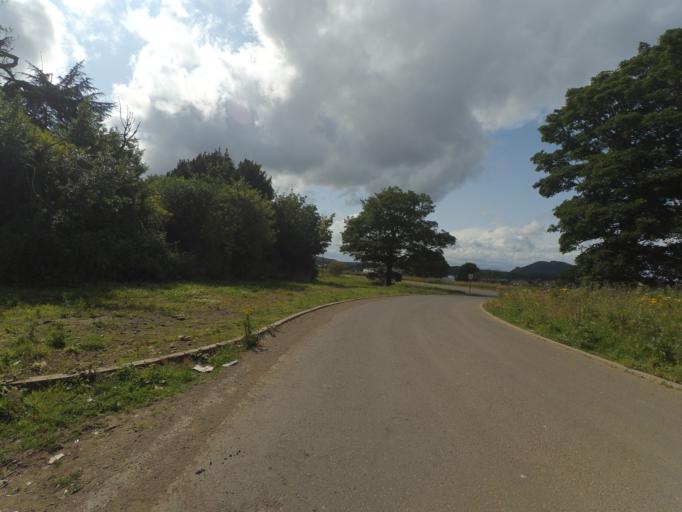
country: GB
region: Scotland
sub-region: Midlothian
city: Bonnyrigg
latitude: 55.9178
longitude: -3.1210
